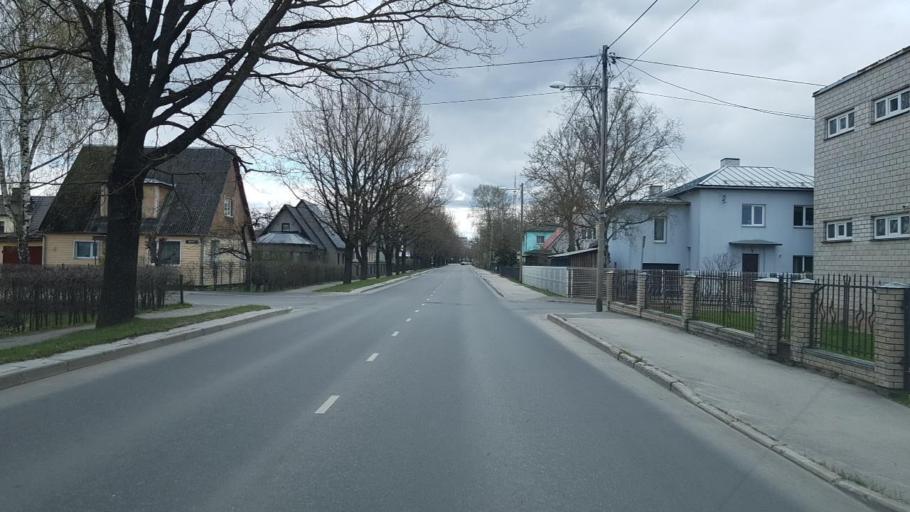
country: EE
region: Tartu
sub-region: Tartu linn
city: Tartu
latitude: 58.3727
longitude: 26.6860
